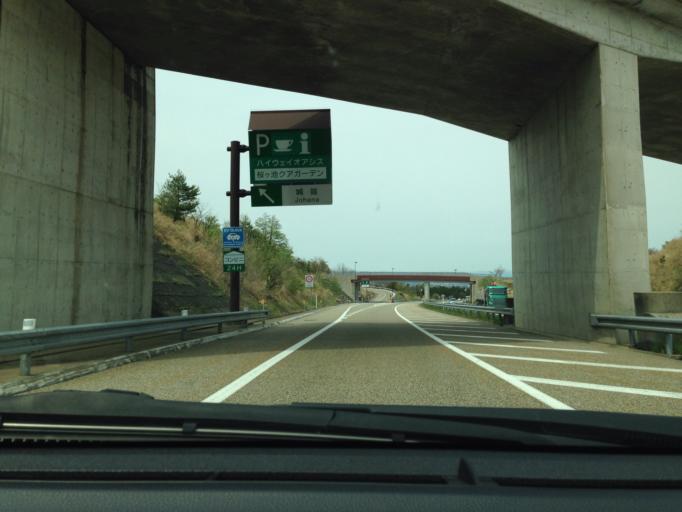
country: JP
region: Toyama
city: Fukumitsu
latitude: 36.5012
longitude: 136.8742
